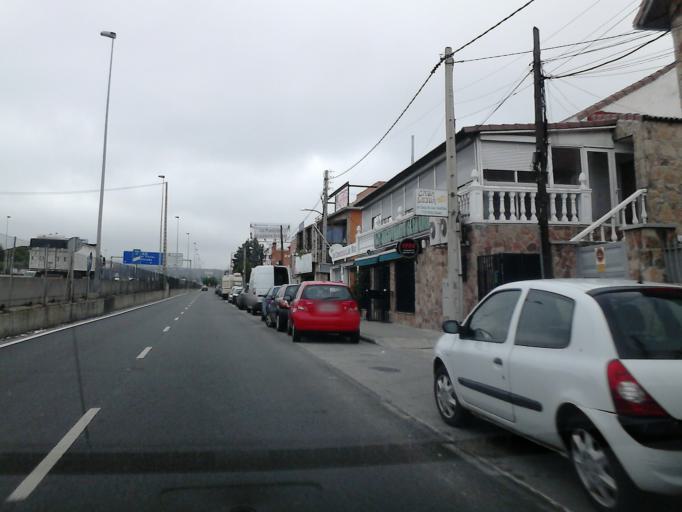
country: ES
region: Madrid
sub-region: Provincia de Madrid
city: Las Matas
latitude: 40.5532
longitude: -3.8980
